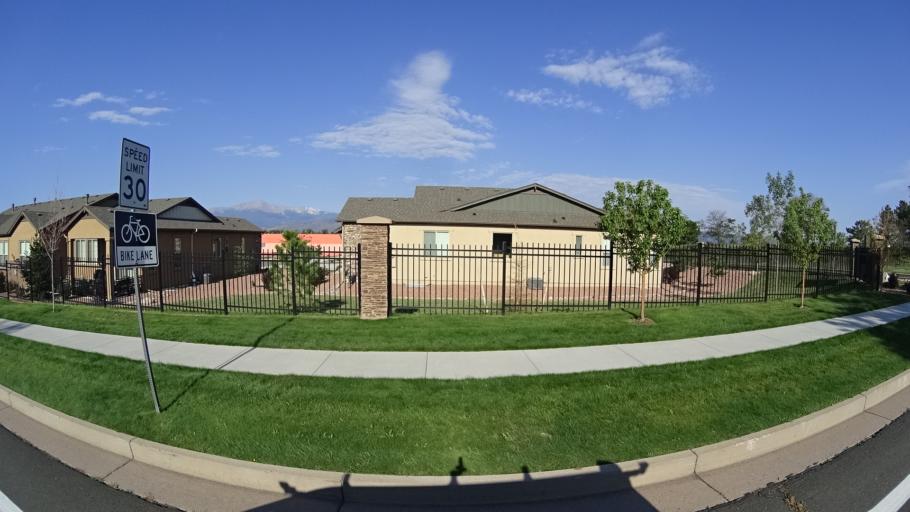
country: US
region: Colorado
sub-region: El Paso County
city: Black Forest
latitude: 38.9472
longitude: -104.7635
